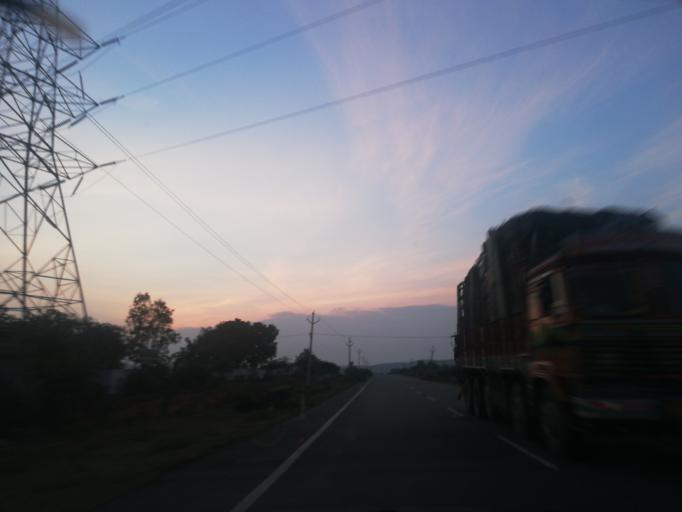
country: IN
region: Andhra Pradesh
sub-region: Guntur
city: Macherla
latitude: 16.6746
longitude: 79.2703
